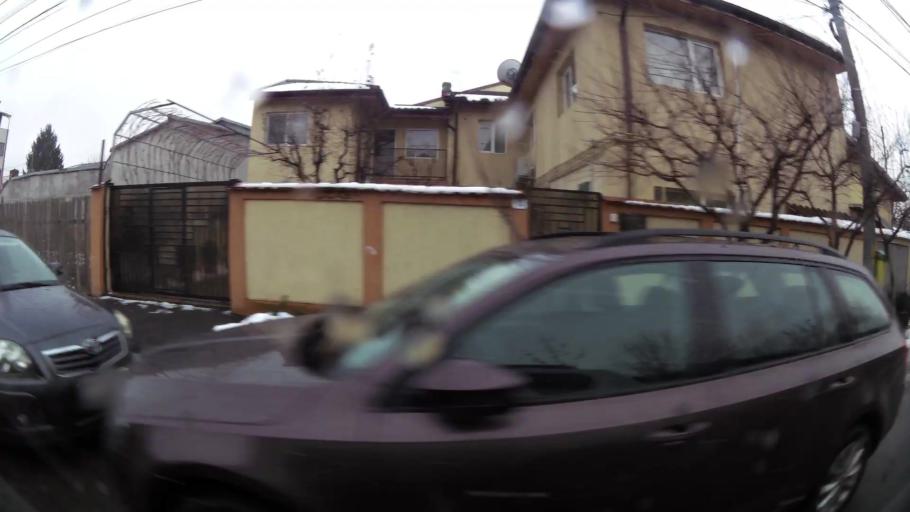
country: RO
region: Ilfov
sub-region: Comuna Mogosoaia
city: Mogosoaia
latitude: 44.4987
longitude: 26.0402
